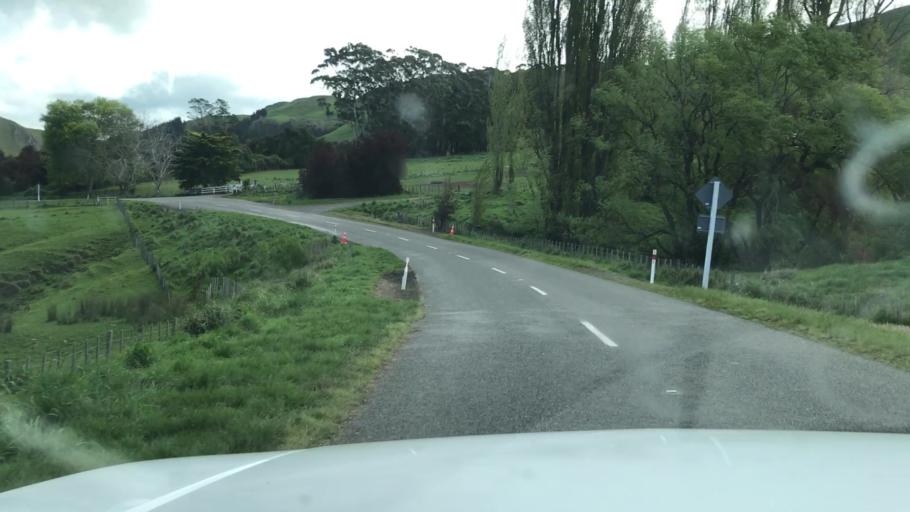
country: NZ
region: Hawke's Bay
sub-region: Hastings District
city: Hastings
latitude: -39.8176
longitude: 176.7445
